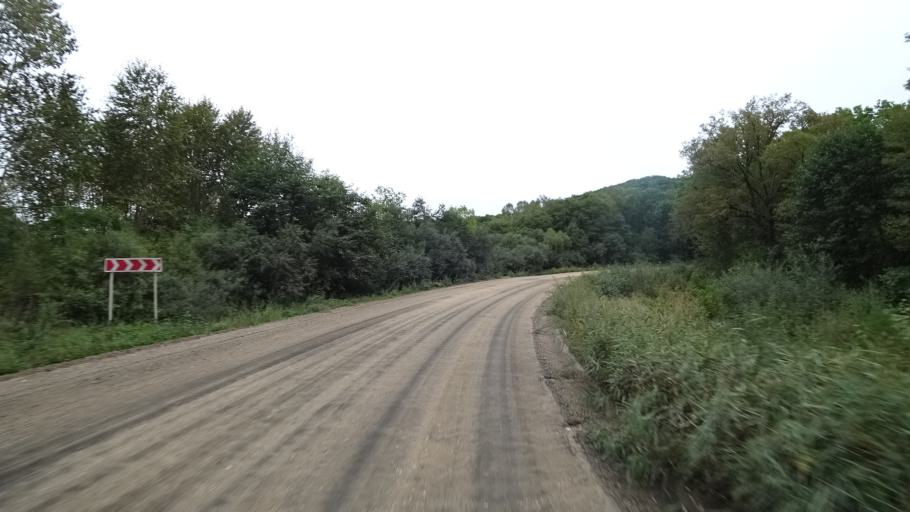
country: RU
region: Primorskiy
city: Rettikhovka
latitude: 44.1806
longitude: 132.8516
